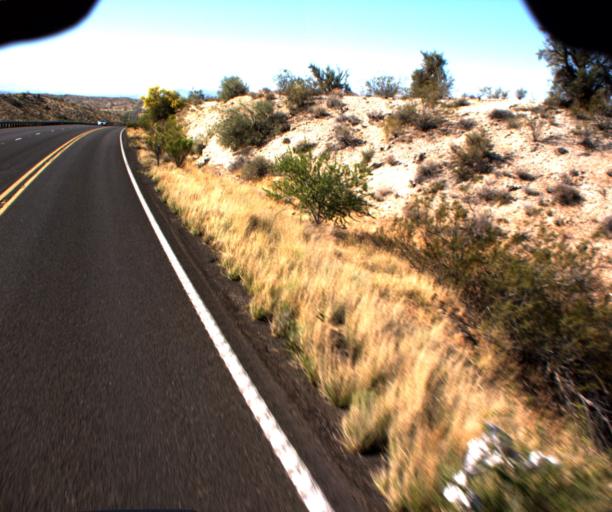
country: US
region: Arizona
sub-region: Mohave County
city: Kingman
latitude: 34.9288
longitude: -113.6590
